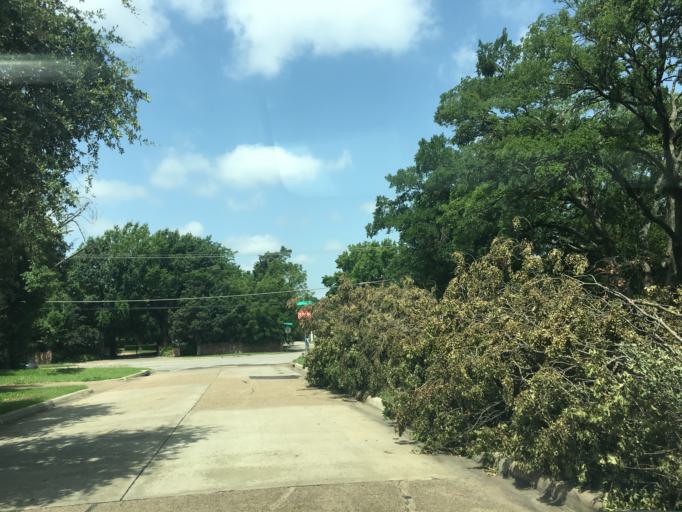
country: US
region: Texas
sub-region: Dallas County
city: University Park
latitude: 32.8770
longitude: -96.8034
